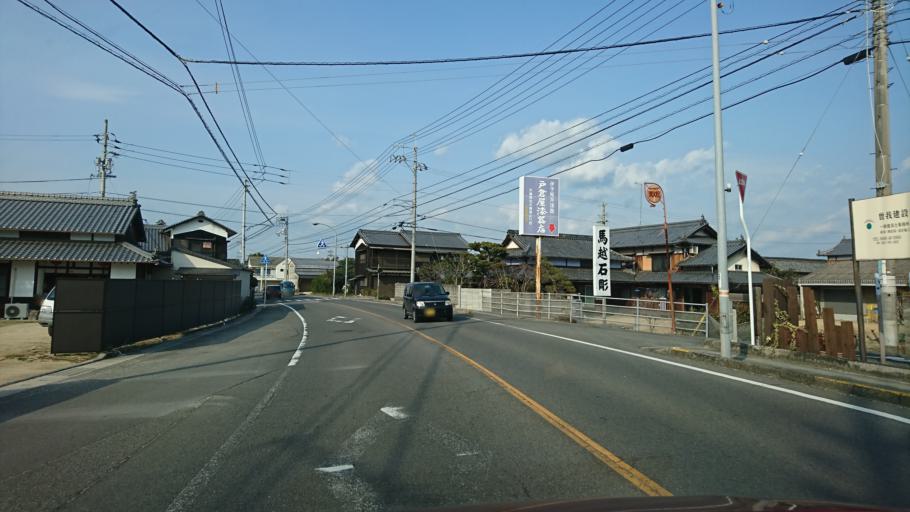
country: JP
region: Ehime
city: Saijo
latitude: 34.0267
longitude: 133.0381
